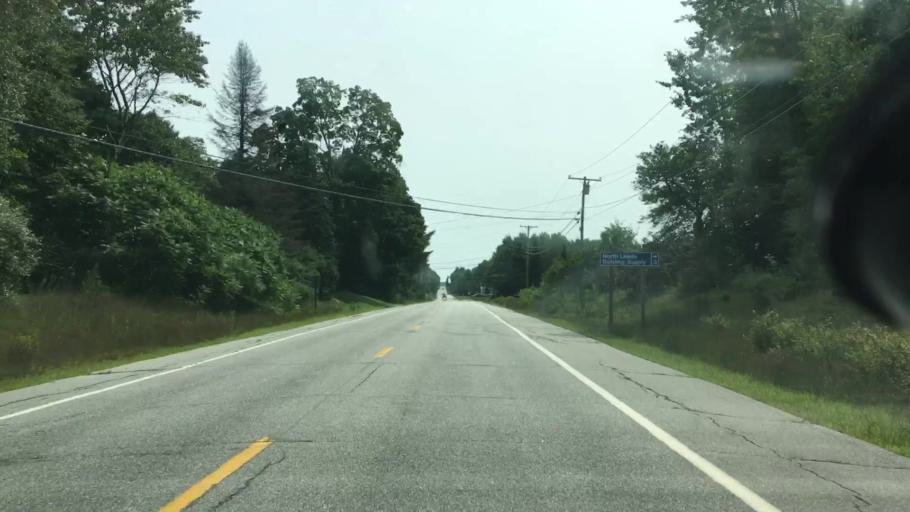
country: US
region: Maine
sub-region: Kennebec County
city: Wayne
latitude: 44.4055
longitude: -70.1328
